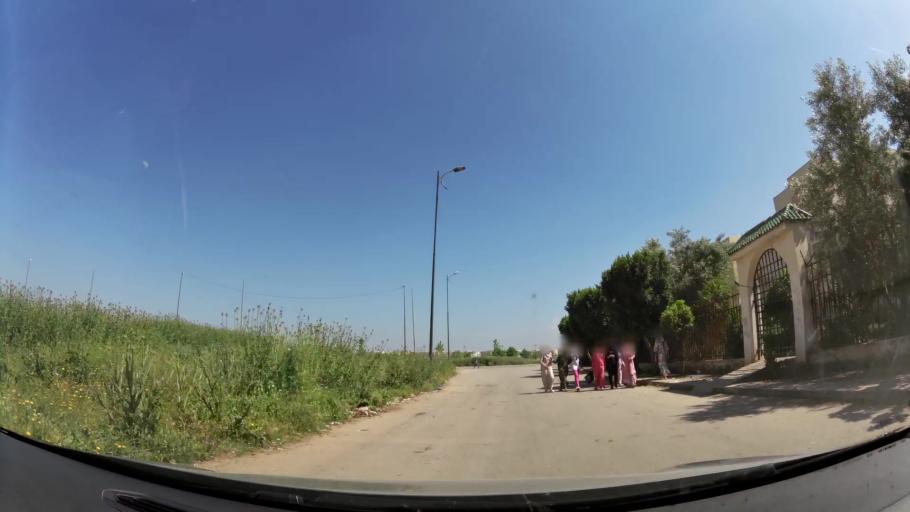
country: MA
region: Fes-Boulemane
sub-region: Fes
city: Fes
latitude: 34.0149
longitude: -5.0216
